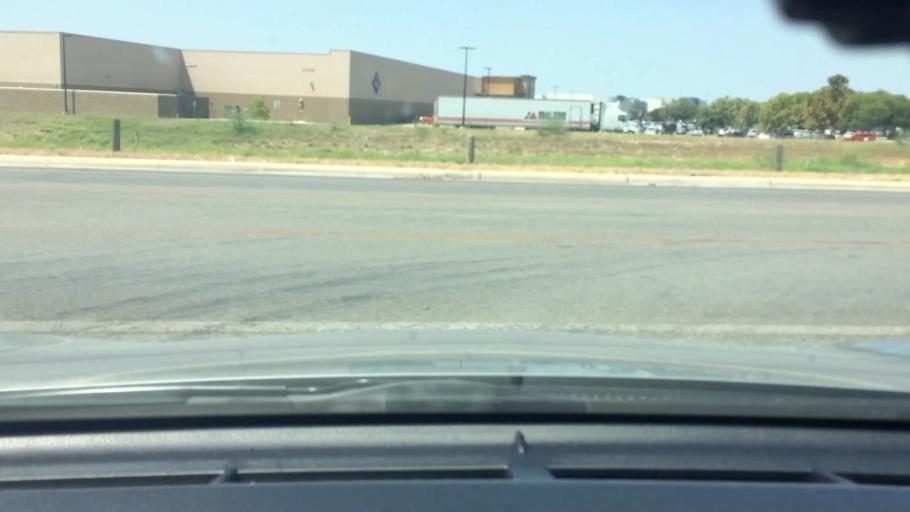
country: US
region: Texas
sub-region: Bexar County
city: China Grove
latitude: 29.3490
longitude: -98.4292
